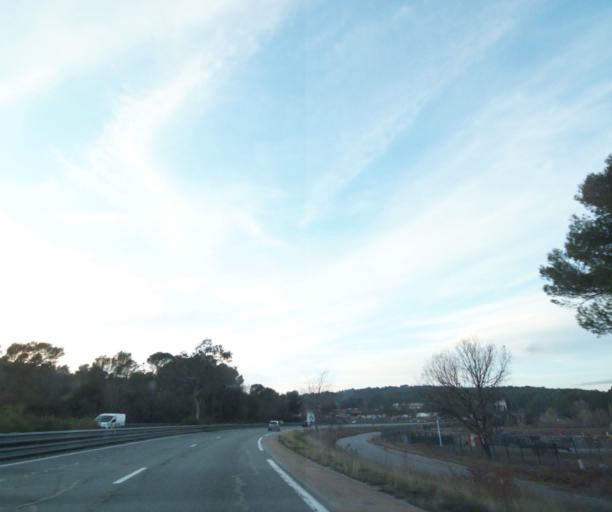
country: FR
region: Provence-Alpes-Cote d'Azur
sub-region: Departement du Var
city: La Motte
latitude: 43.4810
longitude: 6.5120
